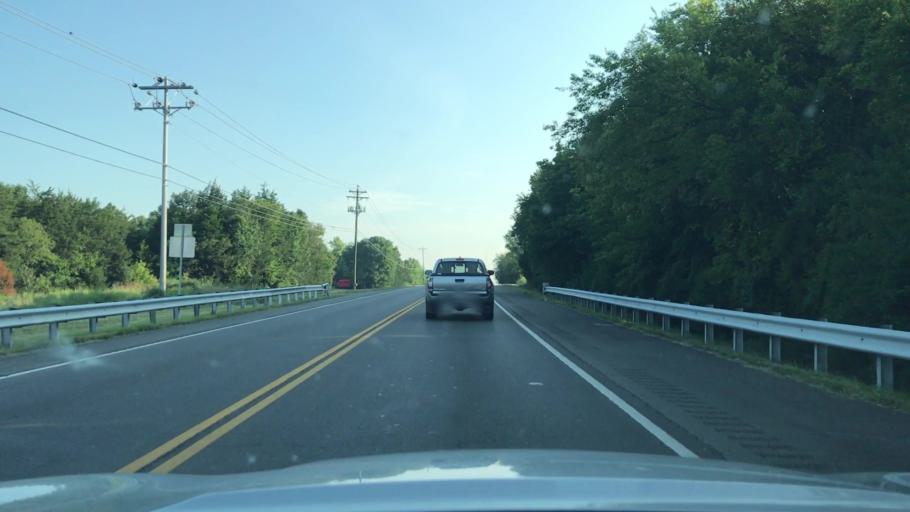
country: US
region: Tennessee
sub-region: Wilson County
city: Mount Juliet
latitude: 36.1567
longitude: -86.5160
